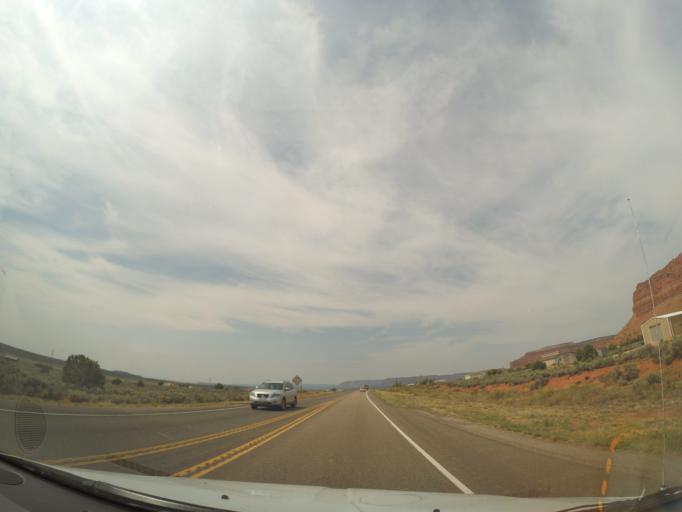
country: US
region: Utah
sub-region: Kane County
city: Kanab
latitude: 37.0233
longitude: -112.4350
